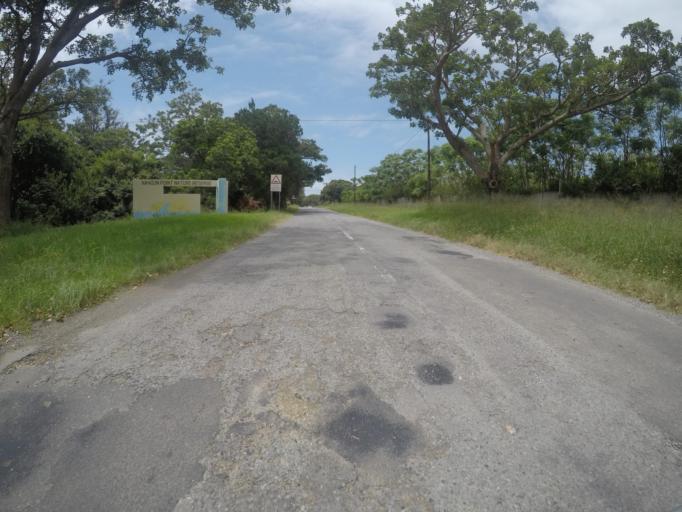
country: ZA
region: Eastern Cape
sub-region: Buffalo City Metropolitan Municipality
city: East London
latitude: -32.9940
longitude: 27.9344
